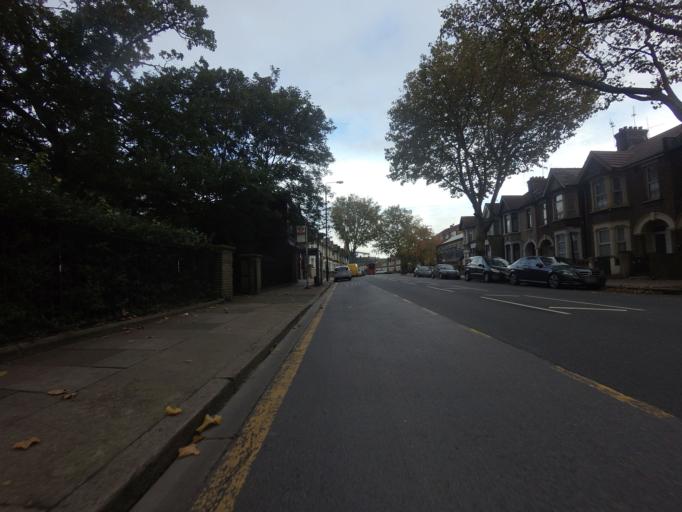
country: GB
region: England
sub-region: Greater London
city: East Ham
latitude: 51.5298
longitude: 0.0559
